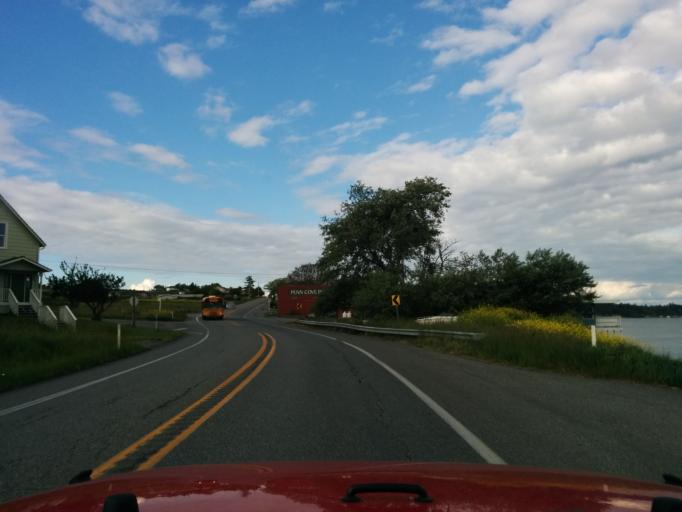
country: US
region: Washington
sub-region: Island County
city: Coupeville
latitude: 48.2344
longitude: -122.7242
